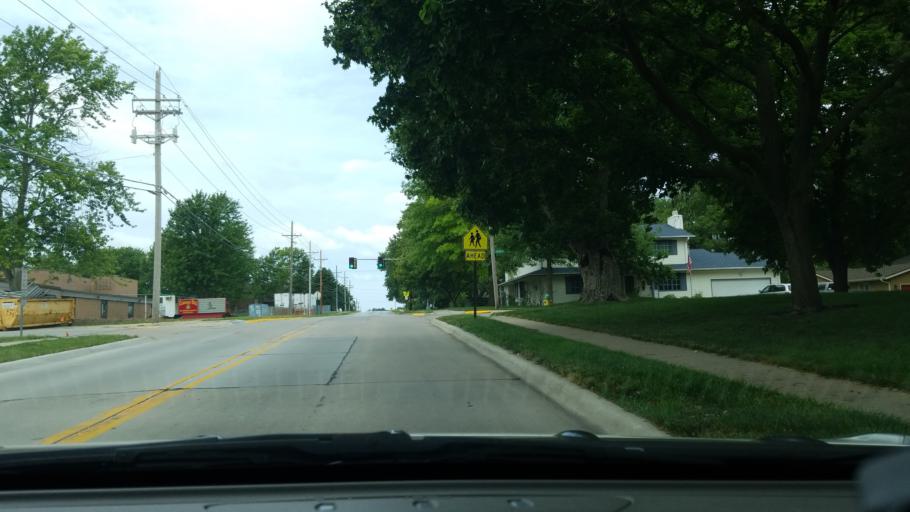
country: US
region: Nebraska
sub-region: Sarpy County
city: Papillion
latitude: 41.1436
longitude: -96.0372
